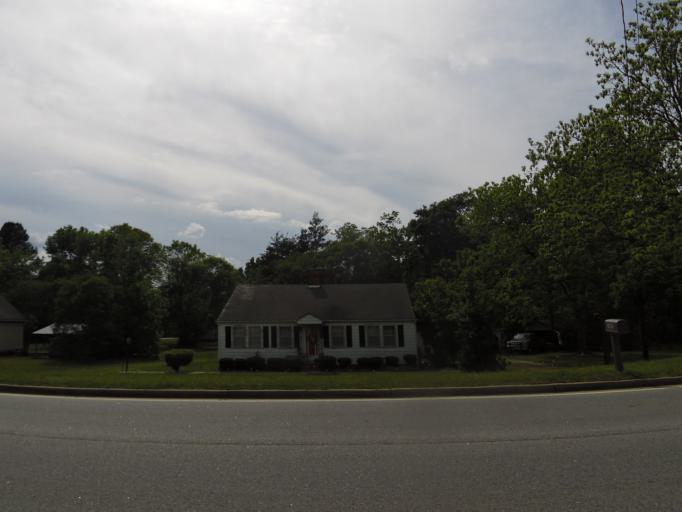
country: US
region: Georgia
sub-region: McDuffie County
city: Thomson
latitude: 33.4999
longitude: -82.5036
